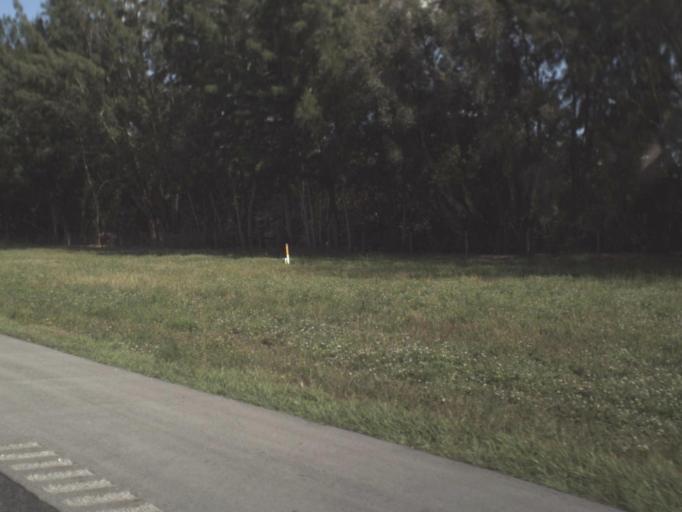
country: US
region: Florida
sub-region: Palm Beach County
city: Kings Point
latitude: 26.4320
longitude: -80.1727
